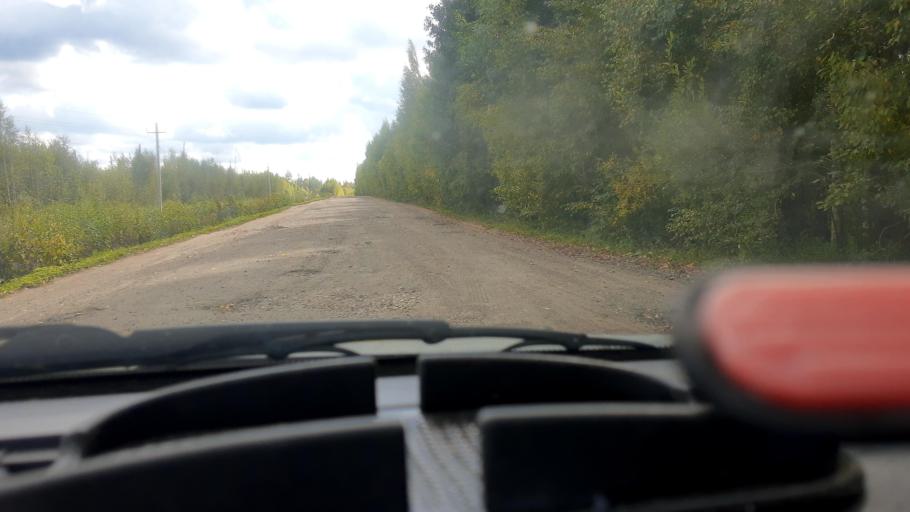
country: RU
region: Mariy-El
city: Kilemary
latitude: 56.8874
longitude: 46.7606
